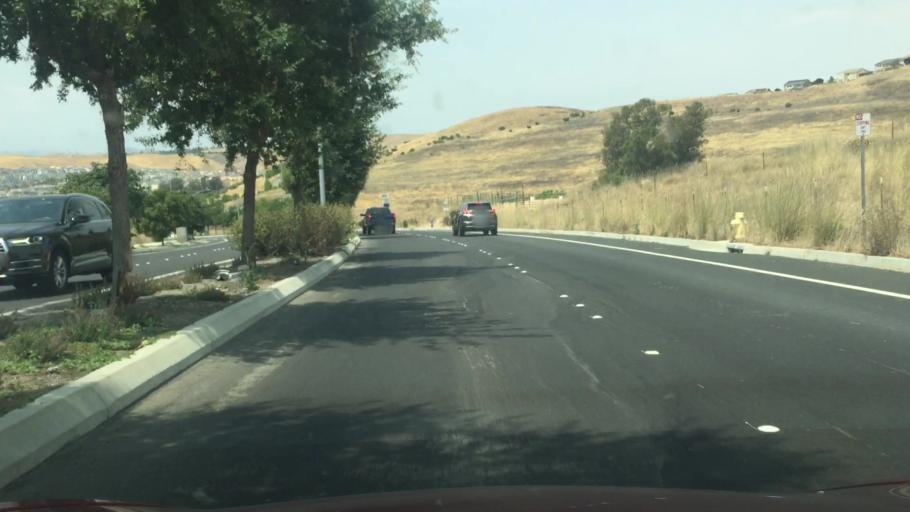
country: US
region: California
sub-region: Alameda County
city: Pleasanton
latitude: 37.7288
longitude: -121.8595
